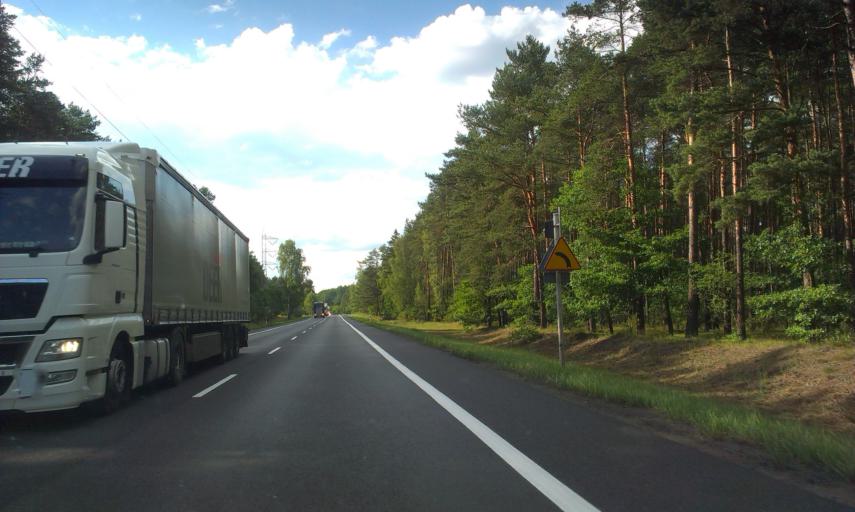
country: PL
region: Greater Poland Voivodeship
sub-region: Powiat pilski
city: Pila
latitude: 53.1762
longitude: 16.7760
